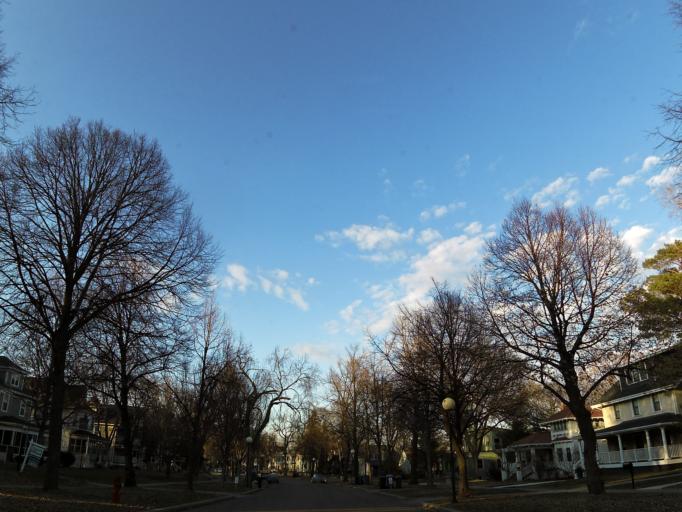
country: US
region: Minnesota
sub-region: Hennepin County
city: Saint Louis Park
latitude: 44.9259
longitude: -93.3122
